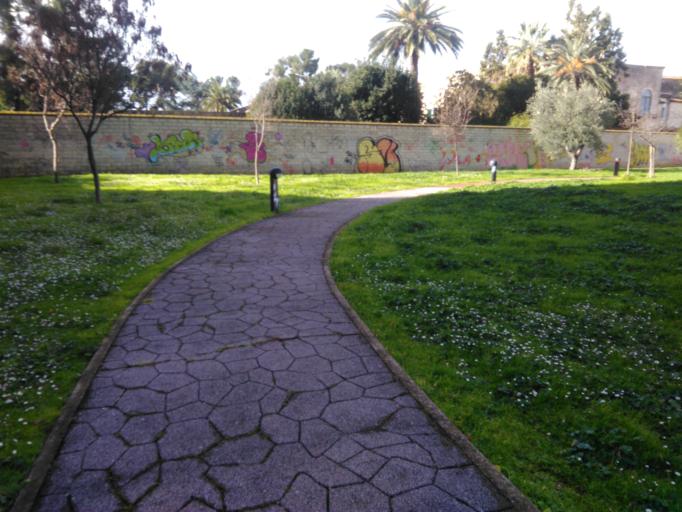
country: IT
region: Apulia
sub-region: Provincia di Barletta - Andria - Trani
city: Andria
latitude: 41.2354
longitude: 16.3053
